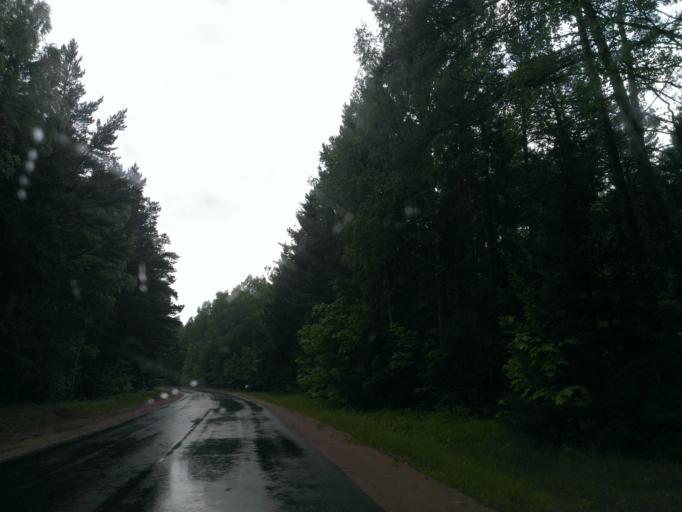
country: LT
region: Klaipedos apskritis
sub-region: Klaipeda
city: Klaipeda
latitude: 55.7927
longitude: 21.0721
